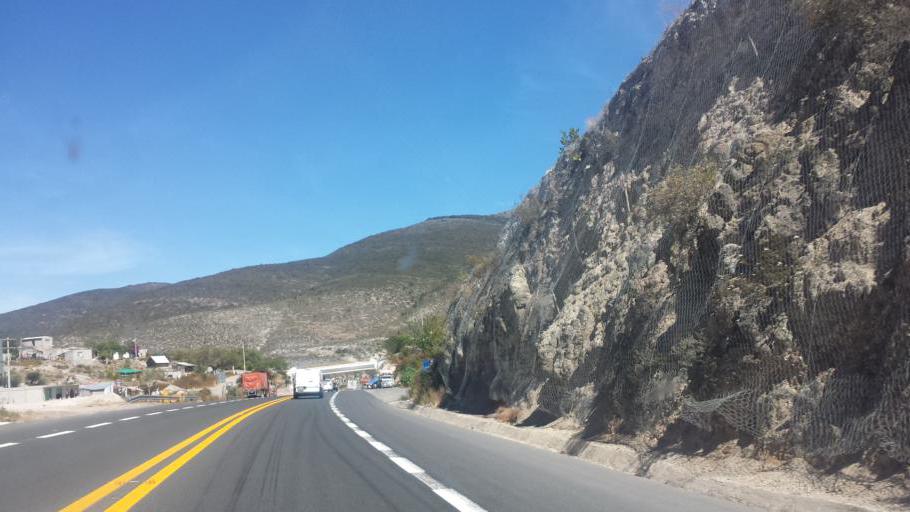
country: MX
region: Oaxaca
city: San Gabriel Casa Blanca
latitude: 17.9781
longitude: -97.3569
